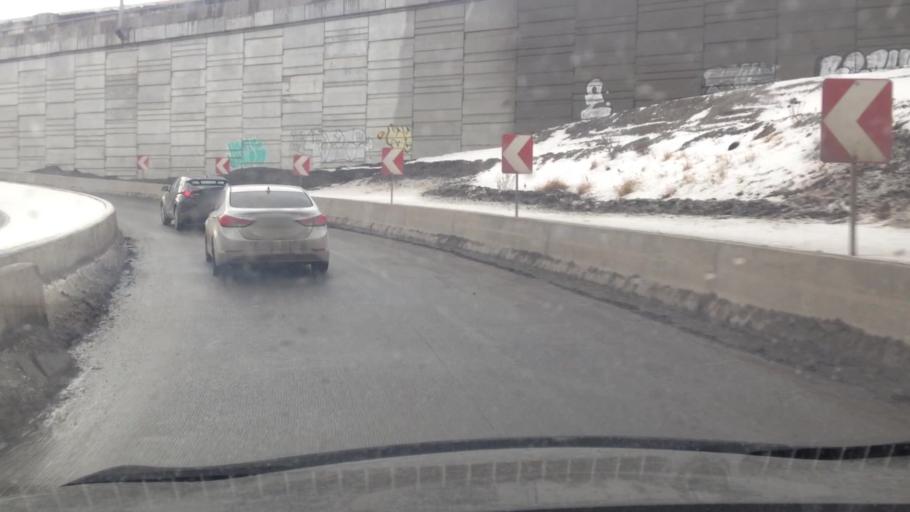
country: CA
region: Quebec
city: Westmount
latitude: 45.4826
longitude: -73.5861
